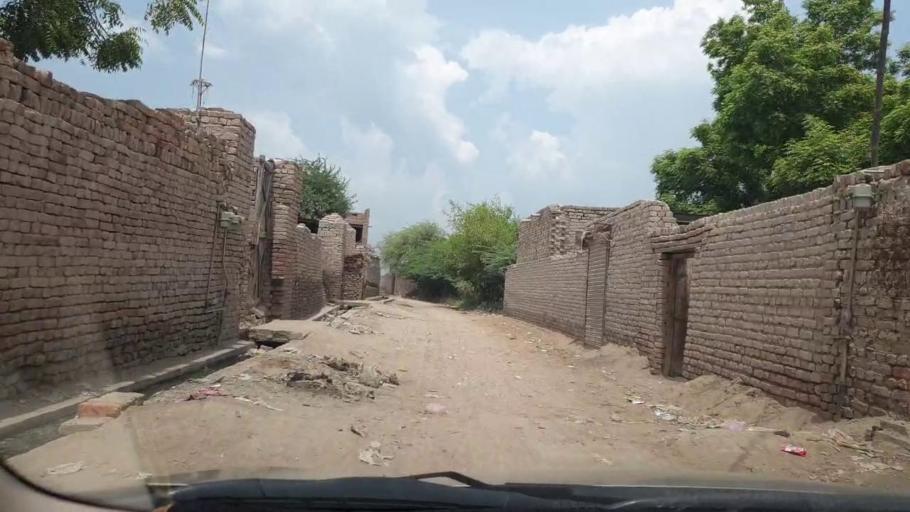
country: PK
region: Sindh
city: Larkana
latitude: 27.5673
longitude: 68.1262
